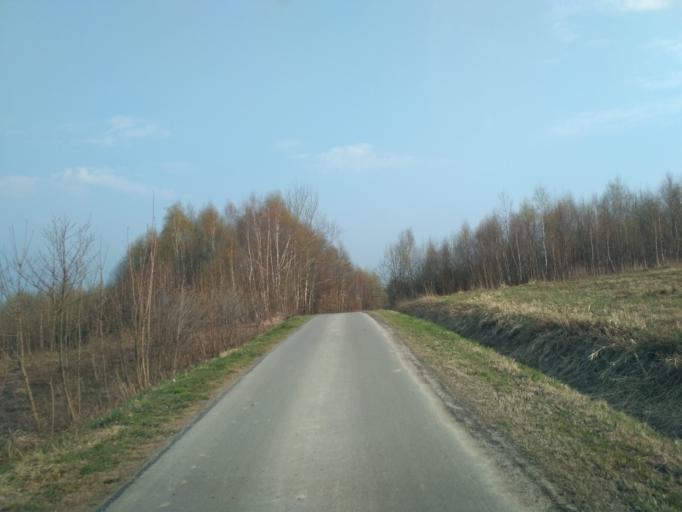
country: PL
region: Subcarpathian Voivodeship
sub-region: Powiat ropczycko-sedziszowski
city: Wielopole Skrzynskie
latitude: 49.9008
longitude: 21.6082
